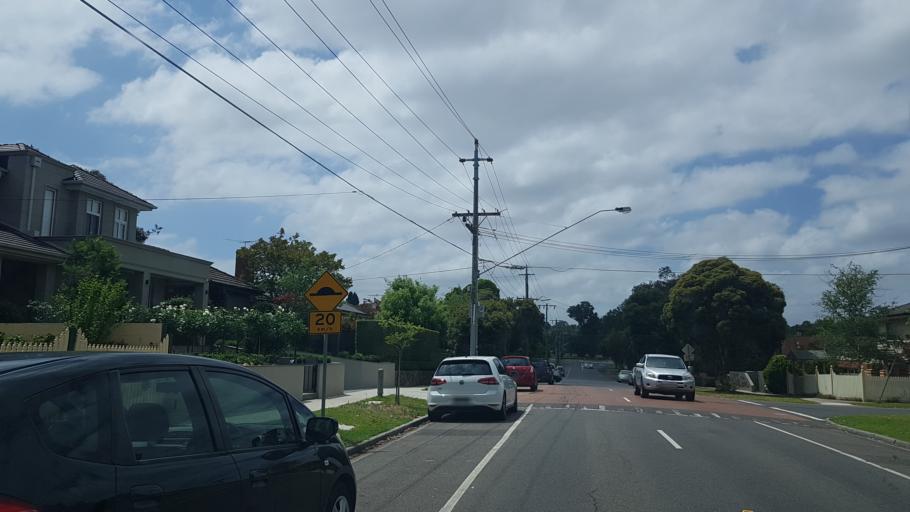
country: AU
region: Victoria
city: Rosanna
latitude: -37.7494
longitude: 145.0684
